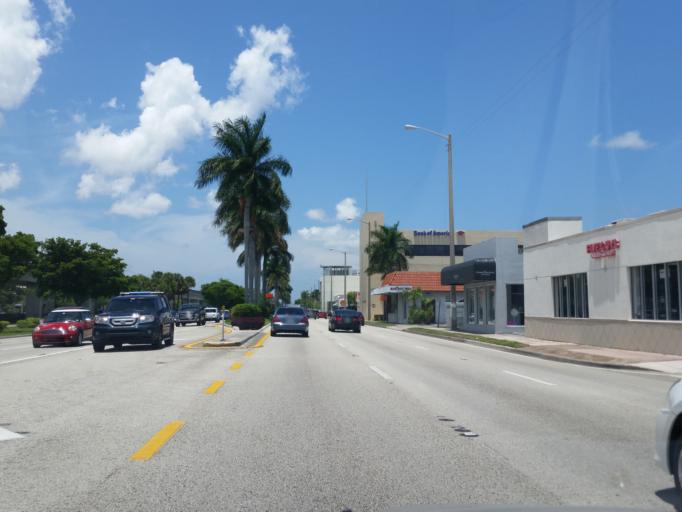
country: US
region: Florida
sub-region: Miami-Dade County
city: South Miami
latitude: 25.7088
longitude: -80.2839
